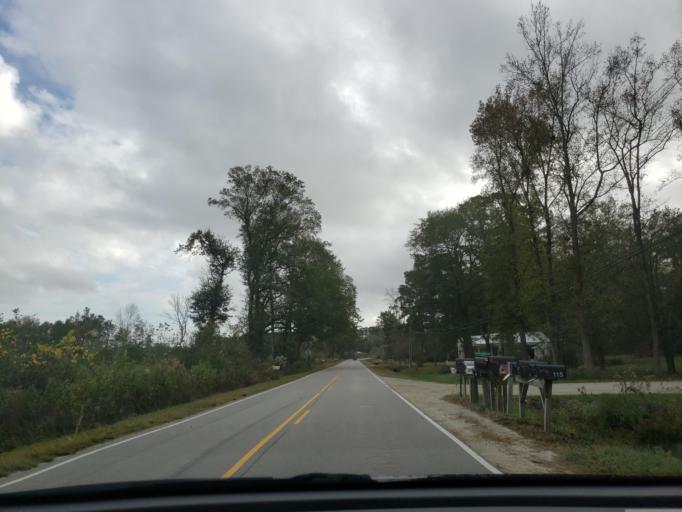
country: US
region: North Carolina
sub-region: Onslow County
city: Jacksonville
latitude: 34.7192
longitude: -77.5784
